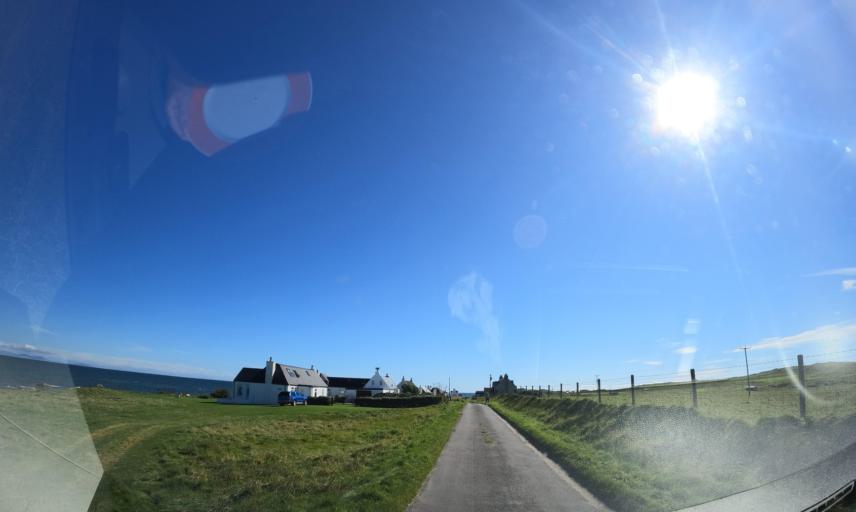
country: GB
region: Scotland
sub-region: Eilean Siar
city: Barra
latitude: 56.4617
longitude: -6.8937
